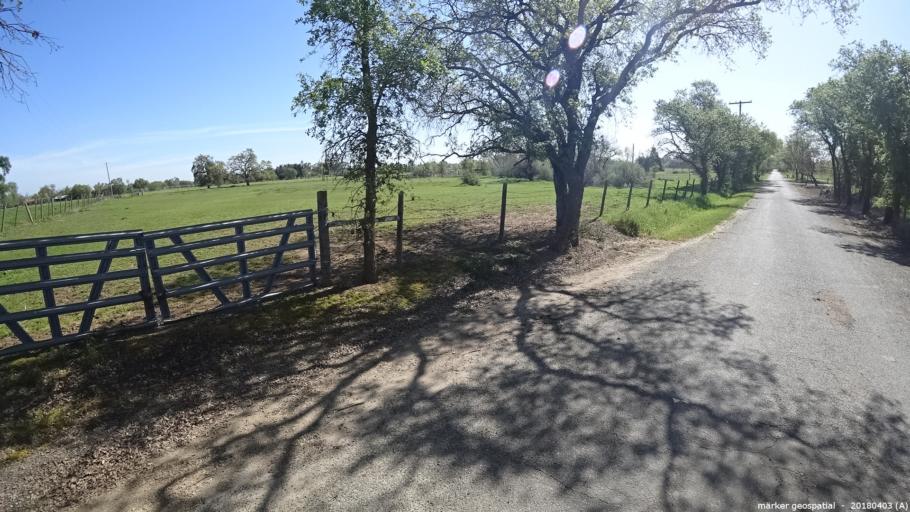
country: US
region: California
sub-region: Sacramento County
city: Wilton
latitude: 38.4324
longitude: -121.2114
